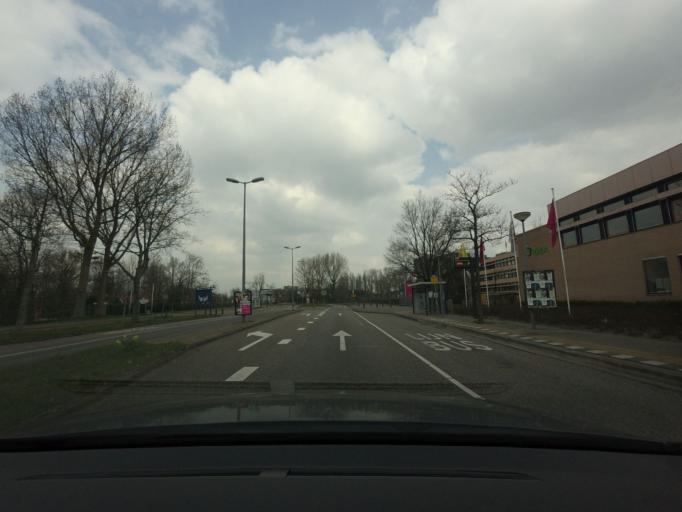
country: NL
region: North Holland
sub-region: Gemeente Alkmaar
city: Alkmaar
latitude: 52.6416
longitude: 4.7237
